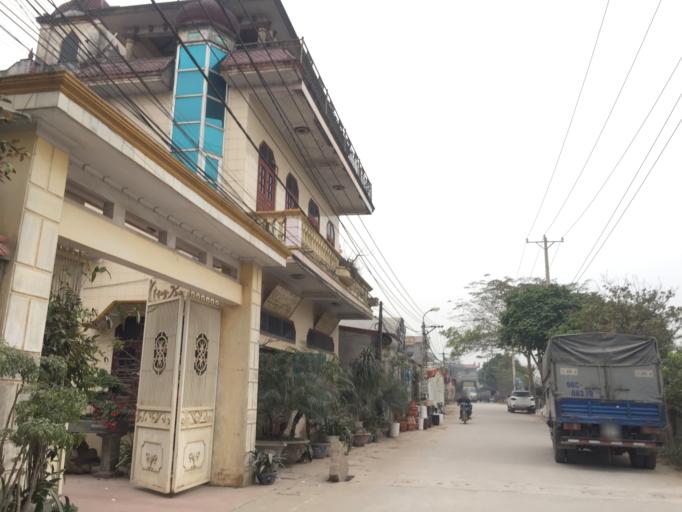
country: VN
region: Hung Yen
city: Van Giang
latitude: 20.9716
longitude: 105.9148
